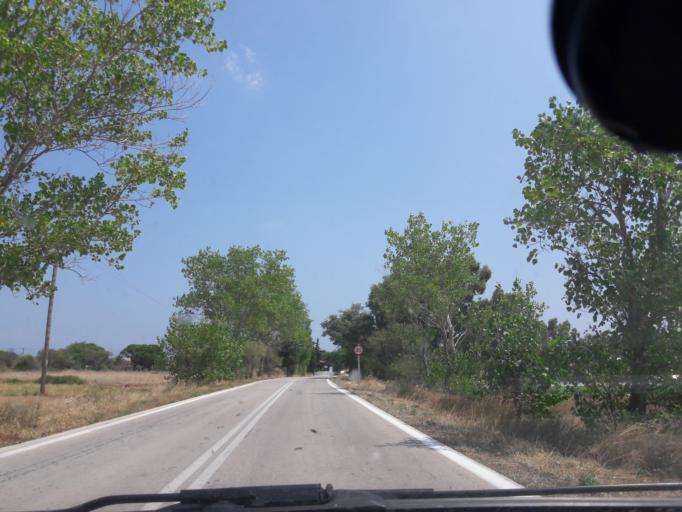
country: GR
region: North Aegean
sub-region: Nomos Lesvou
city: Myrina
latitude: 39.9241
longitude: 25.3285
